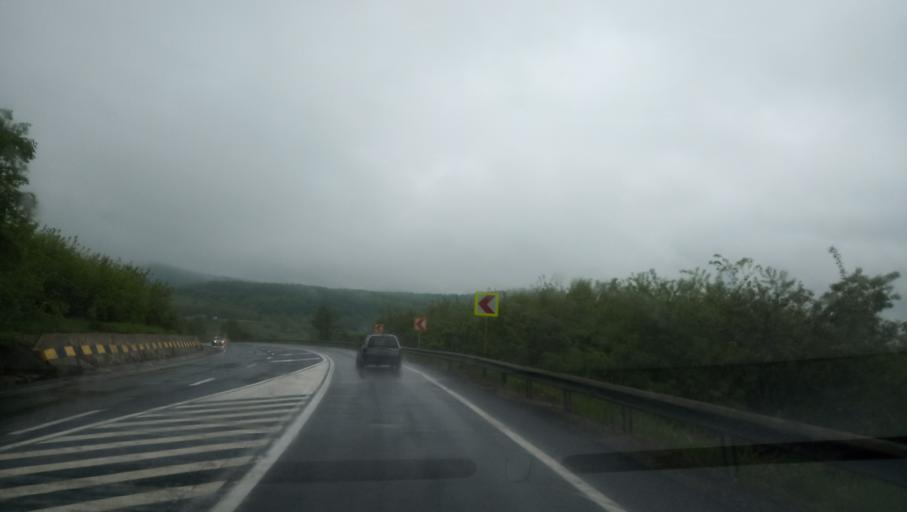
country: RO
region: Sibiu
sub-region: Comuna Tilisca
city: Tilisca
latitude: 45.8132
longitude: 23.8675
